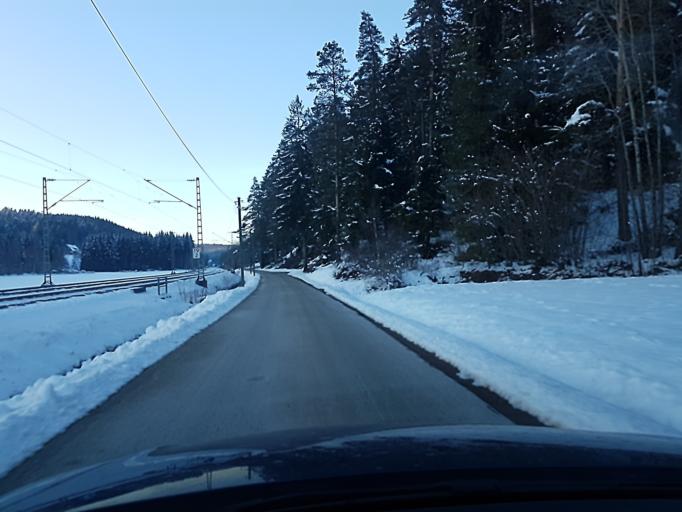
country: DE
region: Baden-Wuerttemberg
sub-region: Freiburg Region
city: Monchweiler
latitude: 48.0908
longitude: 8.4039
